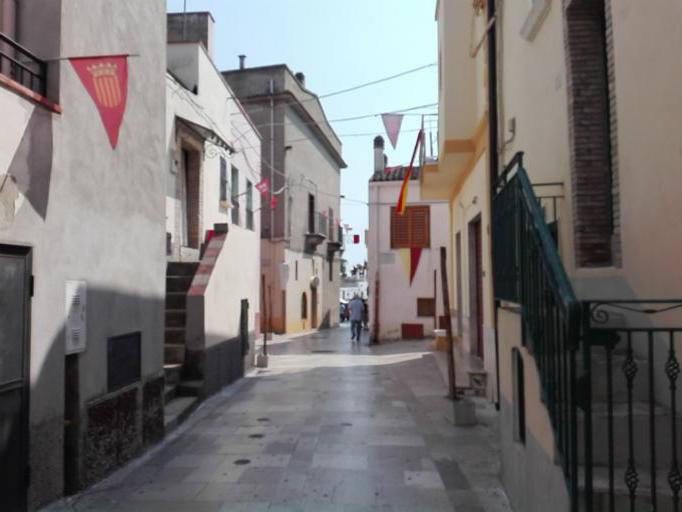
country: IT
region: Basilicate
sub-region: Provincia di Matera
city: Miglionico
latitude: 40.5692
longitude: 16.5007
